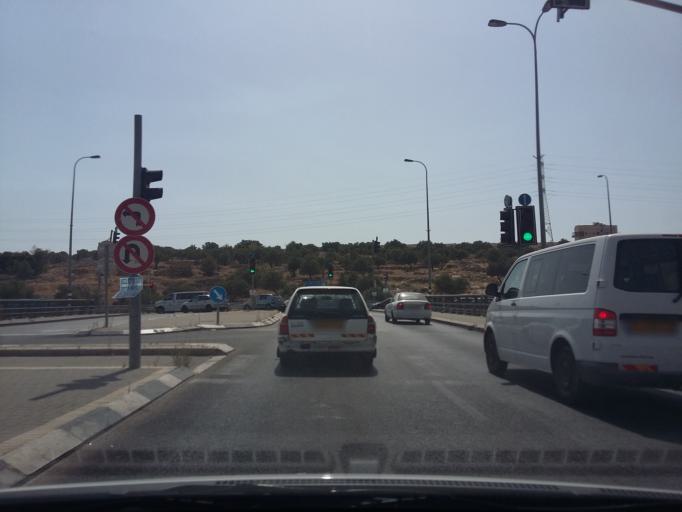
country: PS
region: West Bank
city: Bir Nabala
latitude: 31.8253
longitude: 35.2147
